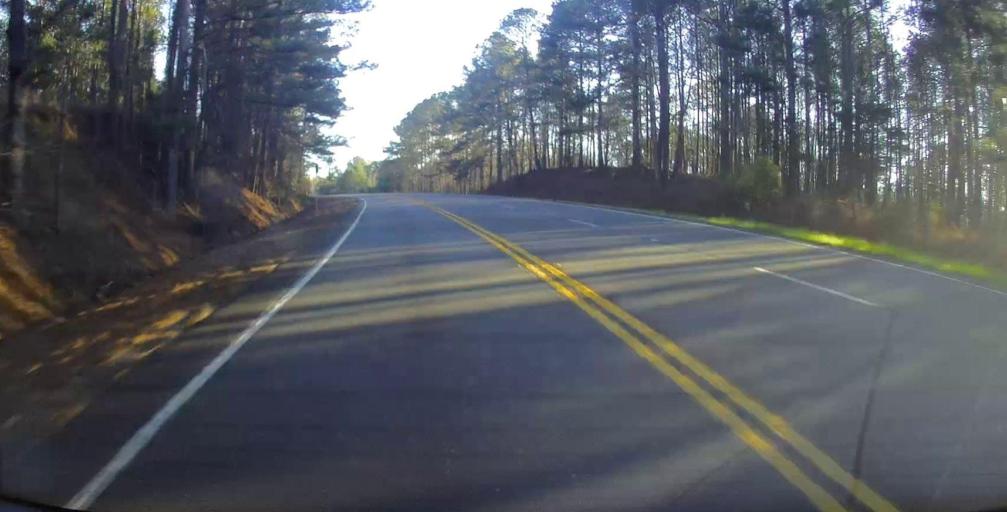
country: US
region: Georgia
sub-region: Talbot County
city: Talbotton
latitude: 32.6492
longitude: -84.5398
